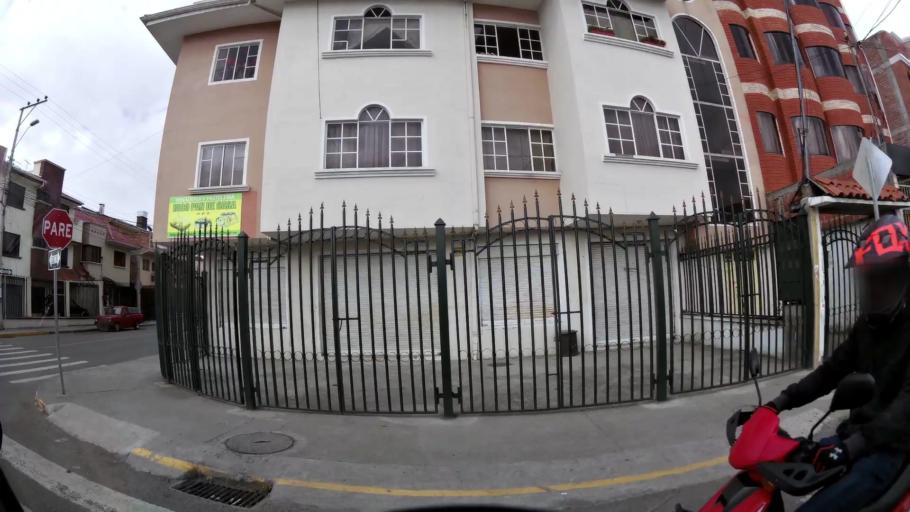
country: EC
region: Azuay
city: Cuenca
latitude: -2.8918
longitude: -78.9819
